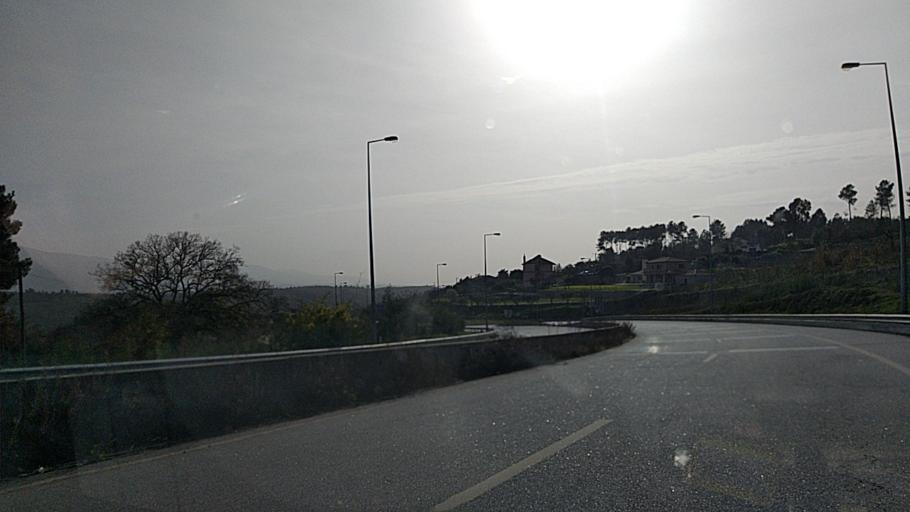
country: PT
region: Guarda
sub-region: Fornos de Algodres
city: Fornos de Algodres
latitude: 40.6136
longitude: -7.5361
